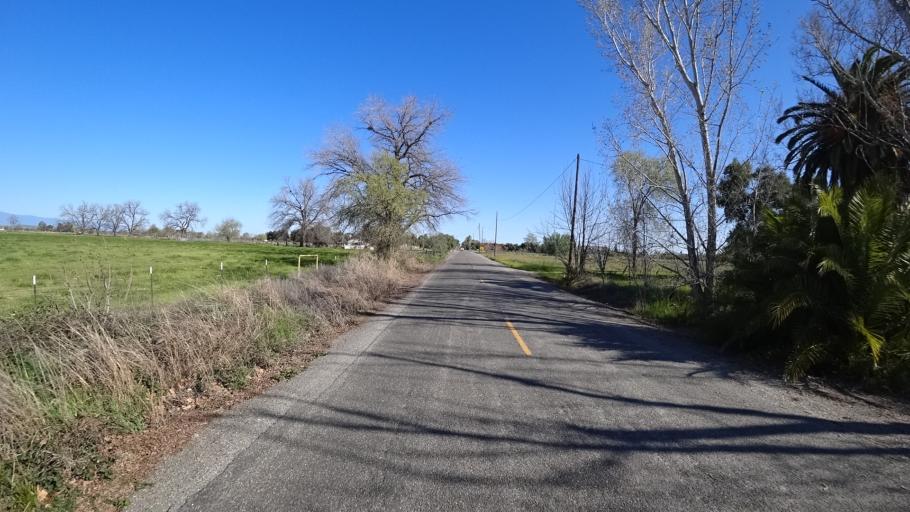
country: US
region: California
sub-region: Glenn County
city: Orland
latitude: 39.7644
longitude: -122.2478
